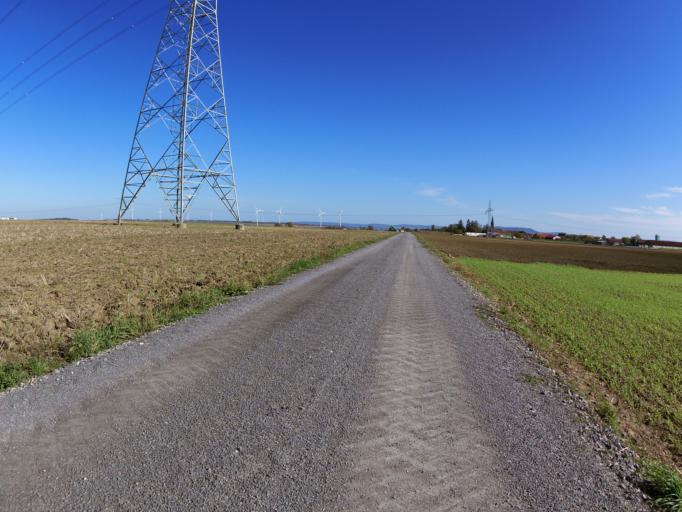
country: DE
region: Bavaria
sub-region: Regierungsbezirk Unterfranken
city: Theilheim
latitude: 49.7458
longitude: 10.0522
